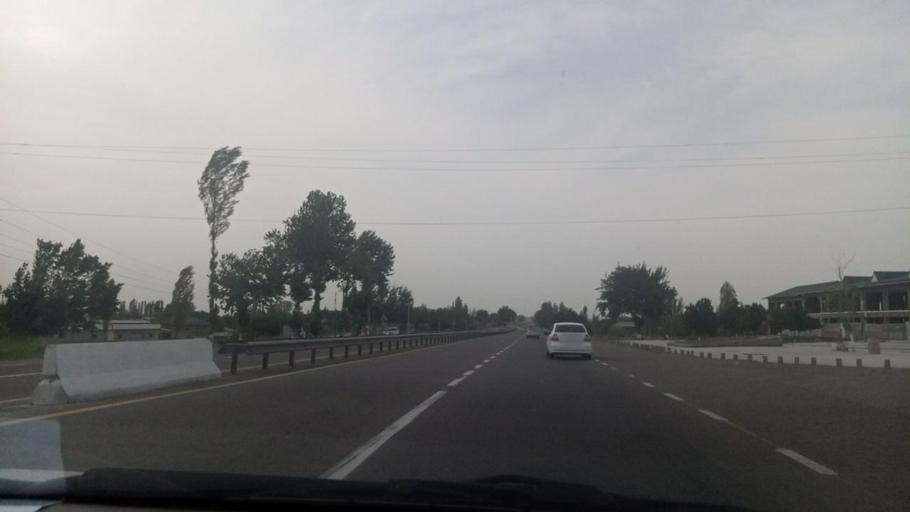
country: UZ
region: Toshkent Shahri
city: Bektemir
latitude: 41.1481
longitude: 69.4293
